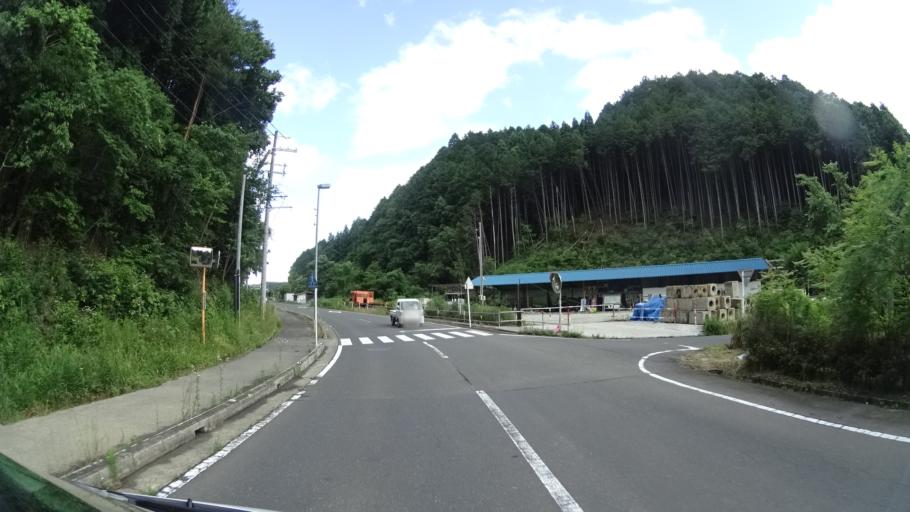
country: JP
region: Kyoto
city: Ayabe
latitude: 35.3619
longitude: 135.2309
